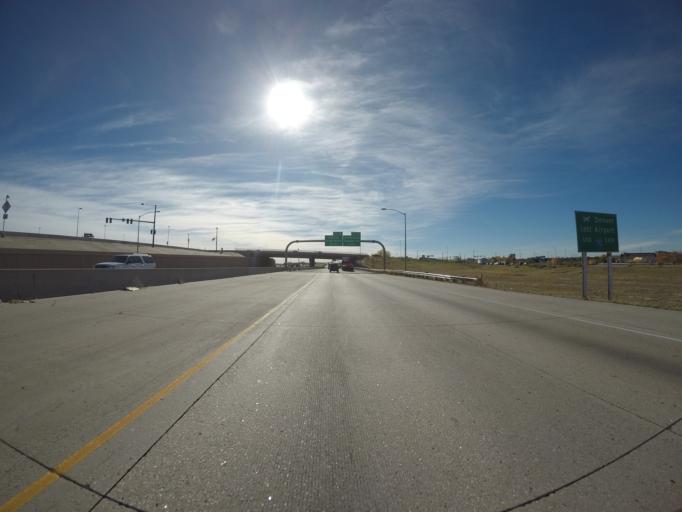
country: US
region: Colorado
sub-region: Adams County
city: Commerce City
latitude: 39.7845
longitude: -104.9018
